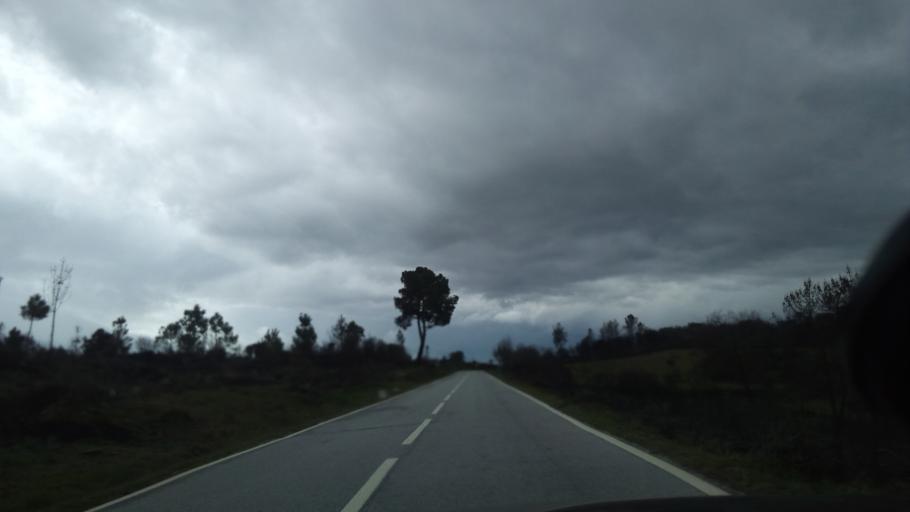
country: PT
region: Guarda
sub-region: Fornos de Algodres
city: Fornos de Algodres
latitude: 40.5772
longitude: -7.5470
